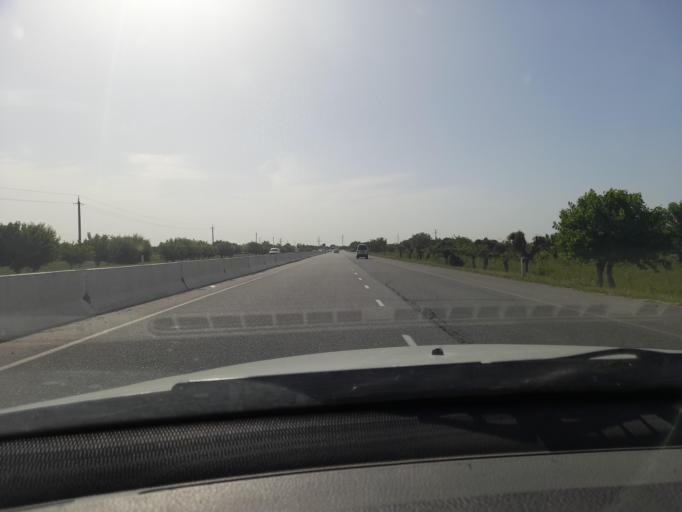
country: UZ
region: Samarqand
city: Ishtixon
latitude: 39.9576
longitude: 66.4690
